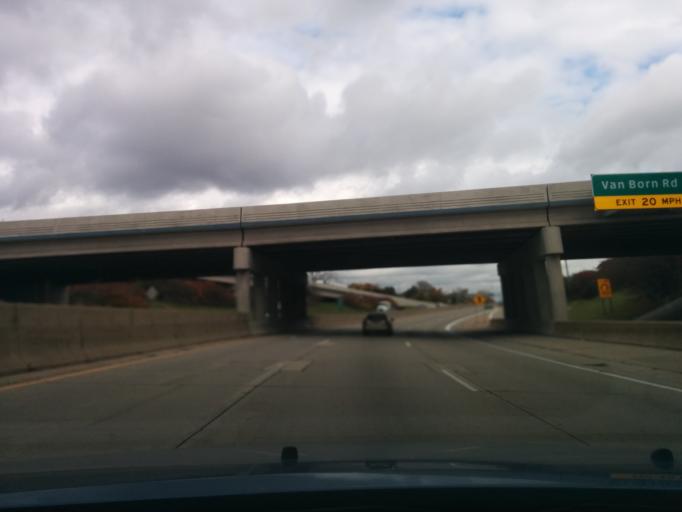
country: US
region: Michigan
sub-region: Wayne County
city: Allen Park
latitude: 42.2690
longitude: -83.2242
